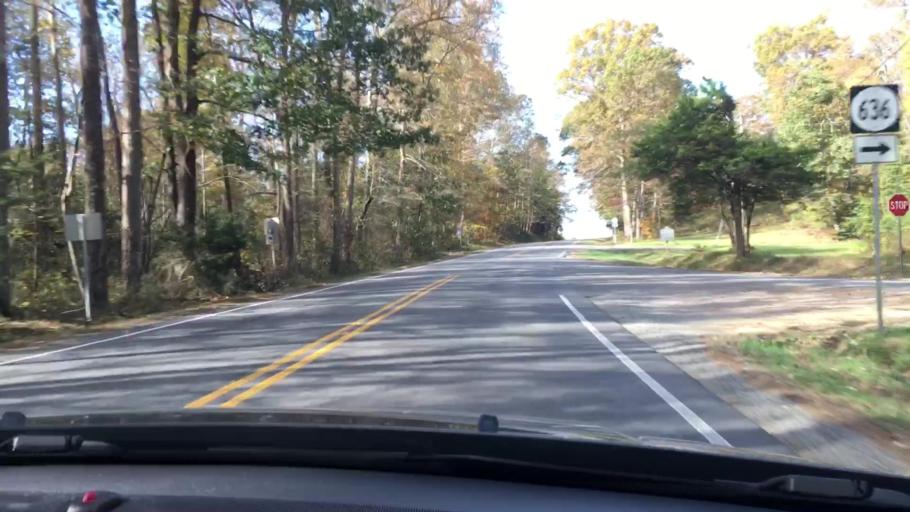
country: US
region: Virginia
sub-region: King William County
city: West Point
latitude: 37.5777
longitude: -76.8449
